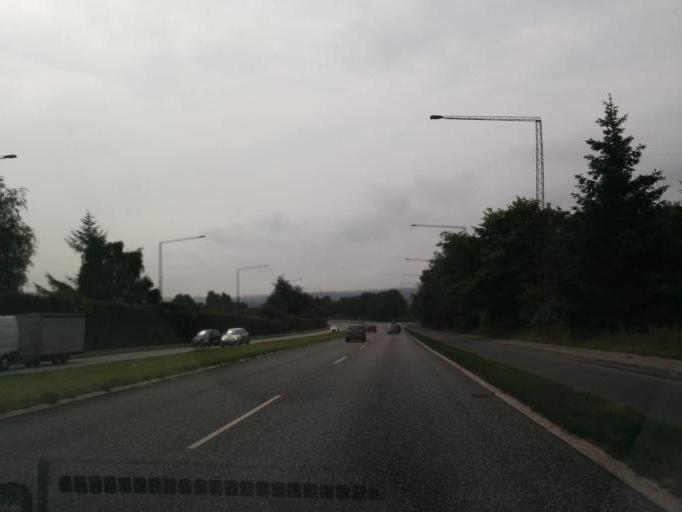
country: DK
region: Central Jutland
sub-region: Arhus Kommune
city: Stavtrup
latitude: 56.1522
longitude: 10.1445
